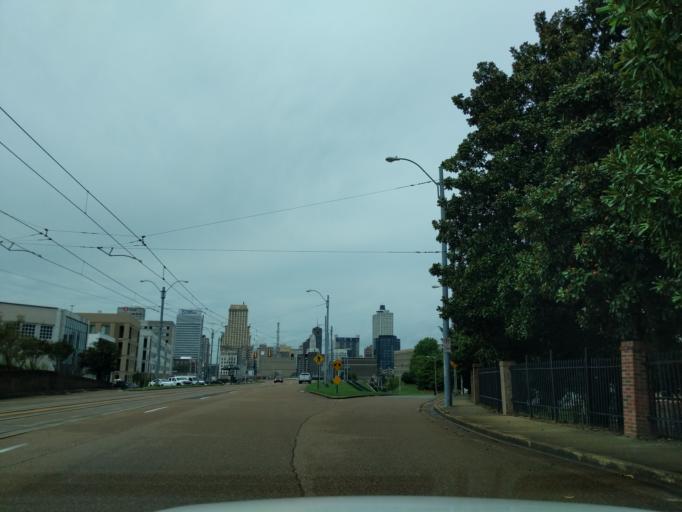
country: US
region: Tennessee
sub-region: Shelby County
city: Memphis
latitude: 35.1422
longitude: -90.0413
